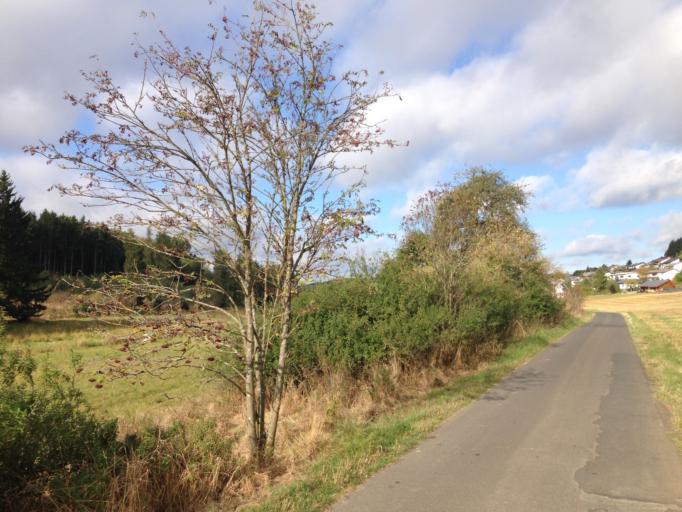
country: DE
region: Hesse
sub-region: Regierungsbezirk Giessen
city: Bischoffen
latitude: 50.6829
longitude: 8.4999
